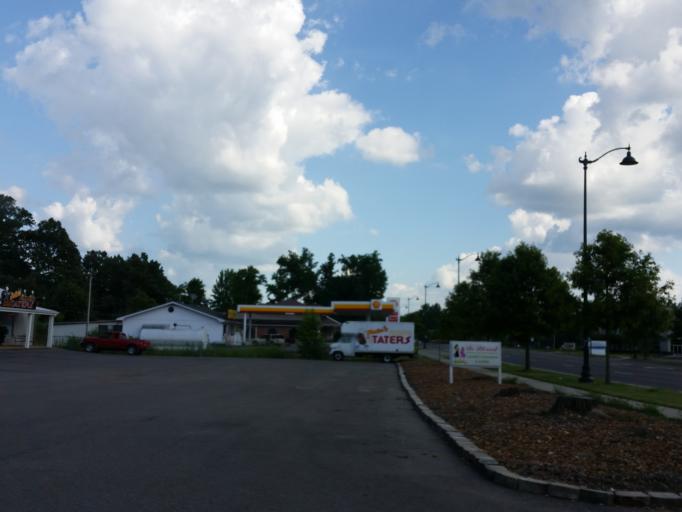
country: US
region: Tennessee
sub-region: Decatur County
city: Parsons
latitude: 35.6455
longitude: -88.1248
